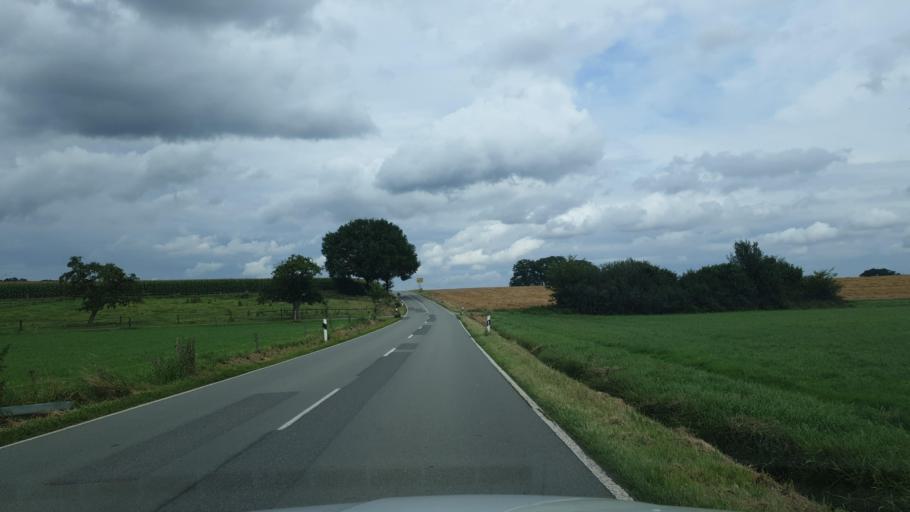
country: DE
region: Lower Saxony
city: Dissen
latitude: 52.1915
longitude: 8.2461
